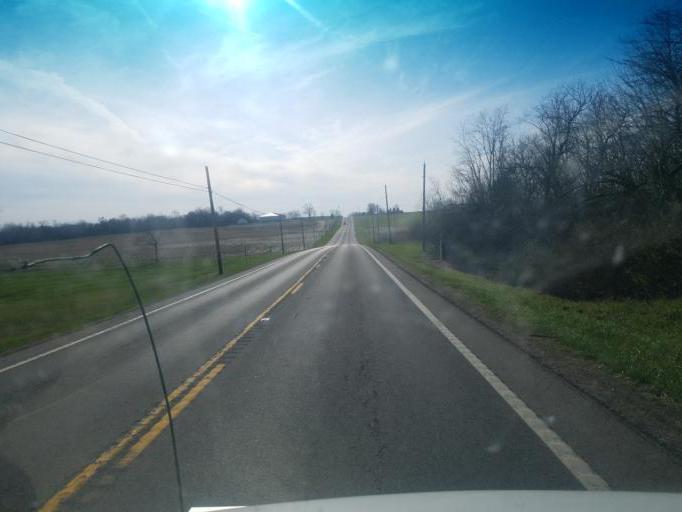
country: US
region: Ohio
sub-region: Logan County
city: Bellefontaine
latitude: 40.3639
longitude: -83.8040
